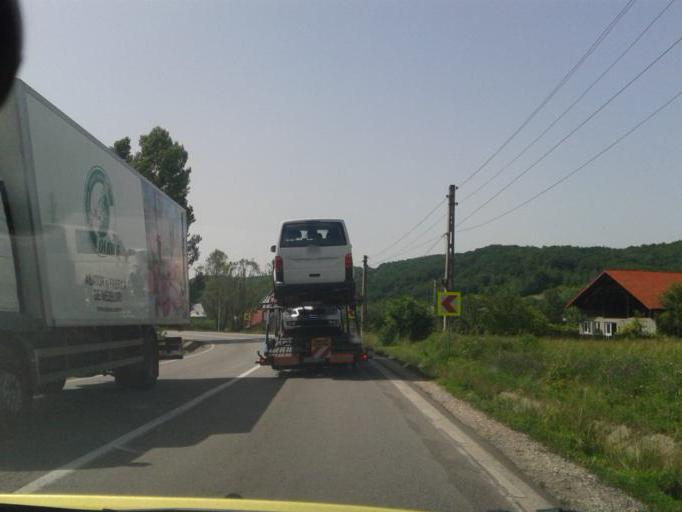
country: RO
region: Arges
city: Draganu-Olteni
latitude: 44.9476
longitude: 24.6990
